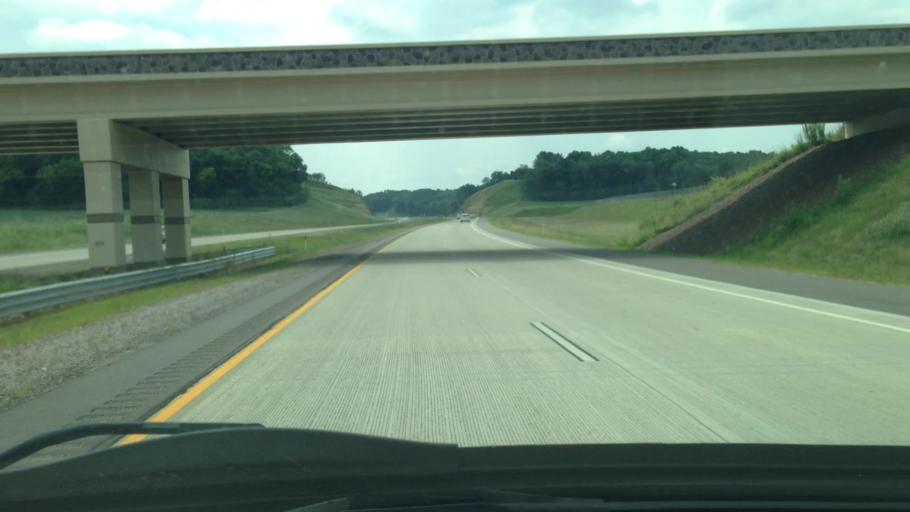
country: US
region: Wisconsin
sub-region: Sauk County
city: West Baraboo
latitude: 43.4459
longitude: -89.7781
